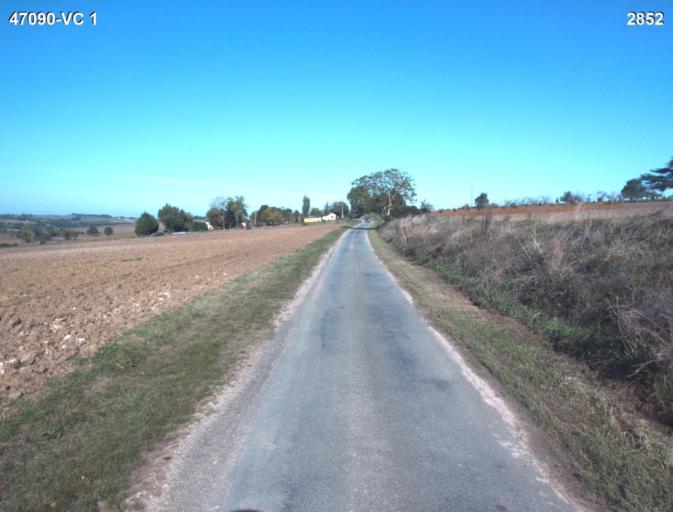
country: FR
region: Aquitaine
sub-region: Departement du Lot-et-Garonne
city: Nerac
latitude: 44.1536
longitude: 0.3964
